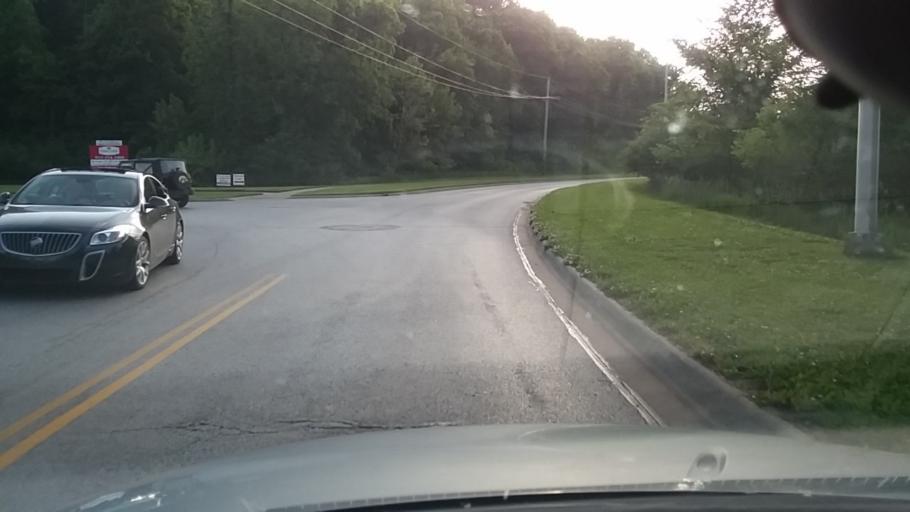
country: US
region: Kansas
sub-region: Johnson County
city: Olathe
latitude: 38.9124
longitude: -94.8638
